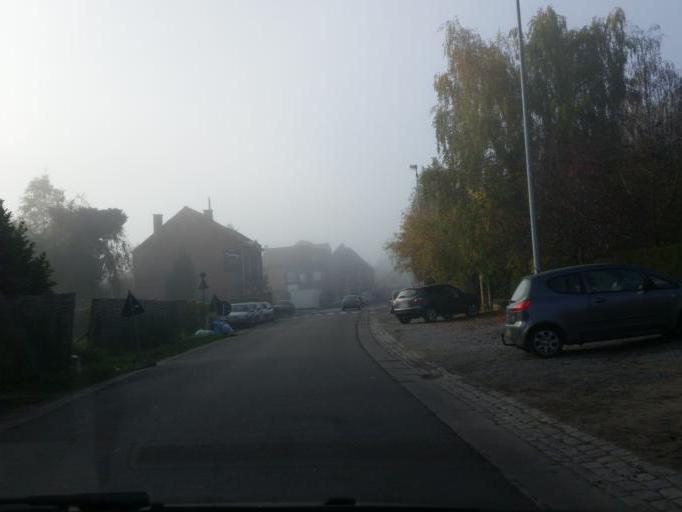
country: BE
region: Flanders
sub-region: Provincie Vlaams-Brabant
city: Opwijk
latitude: 50.9563
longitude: 4.1438
